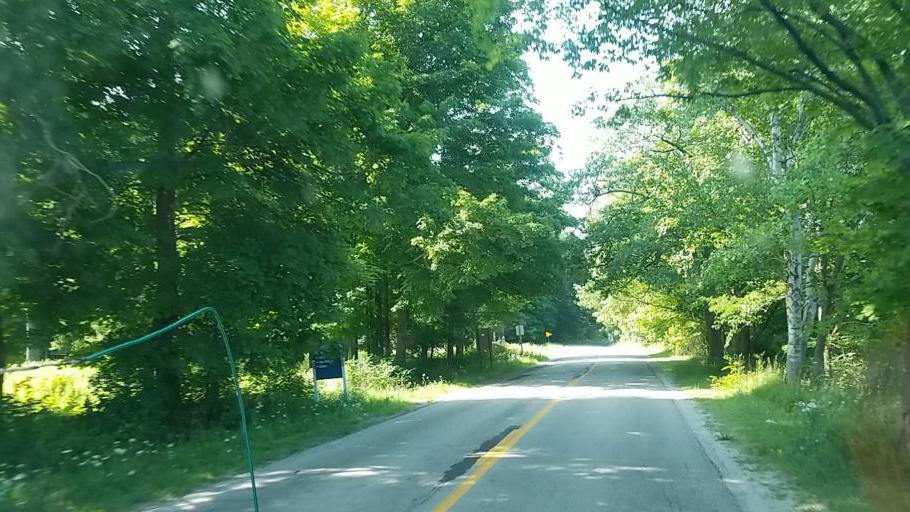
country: US
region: Michigan
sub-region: Muskegon County
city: Whitehall
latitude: 43.3867
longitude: -86.3566
